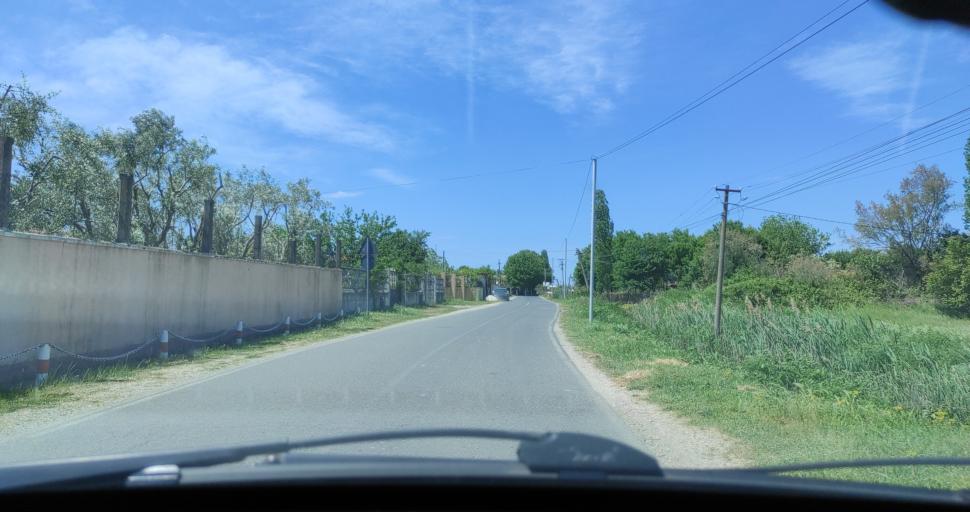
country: AL
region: Lezhe
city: Lezhe
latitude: 41.7564
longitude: 19.6189
